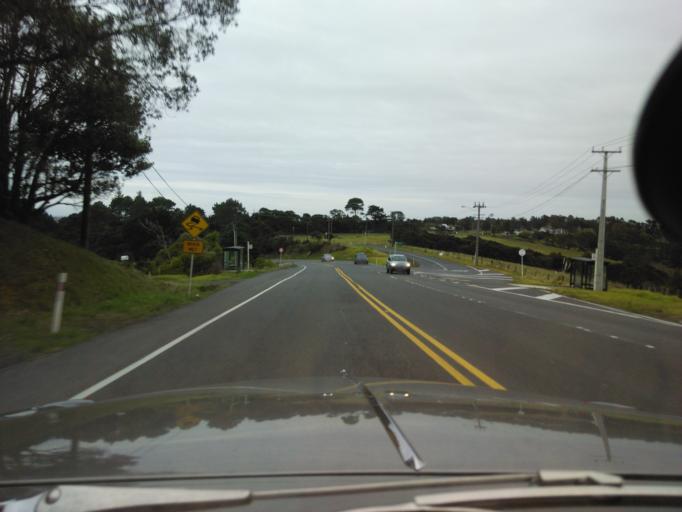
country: NZ
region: Auckland
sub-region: Auckland
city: Rothesay Bay
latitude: -36.7171
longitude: 174.6772
